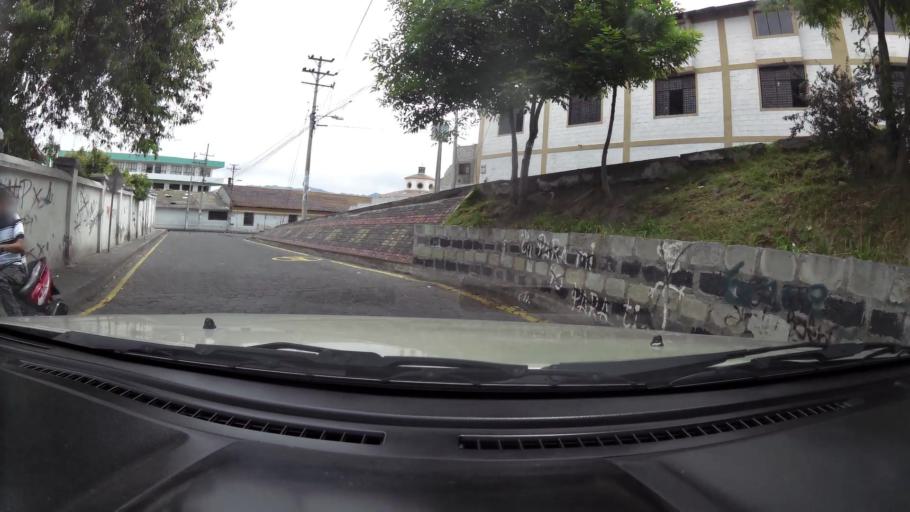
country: EC
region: Cotopaxi
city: Latacunga
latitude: -0.9302
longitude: -78.6170
